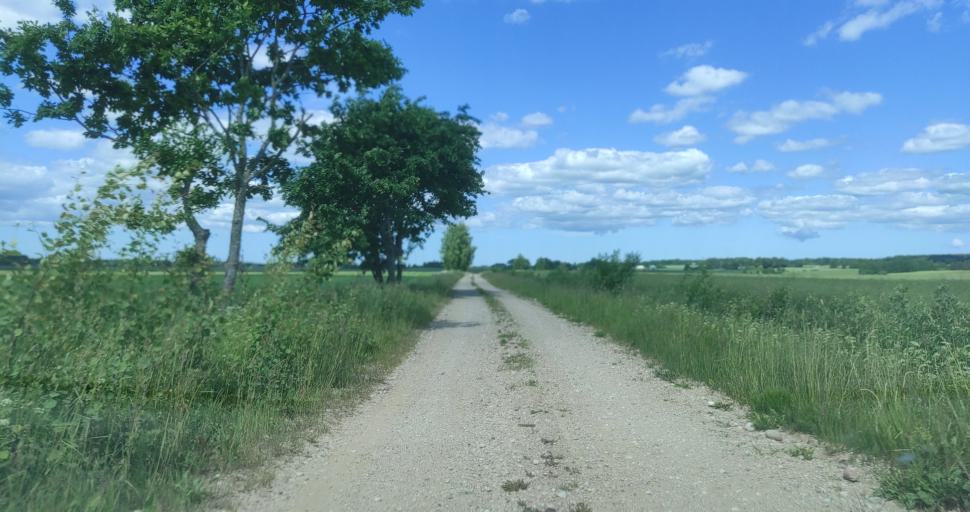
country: LV
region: Aizpute
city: Aizpute
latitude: 56.8607
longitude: 21.7069
